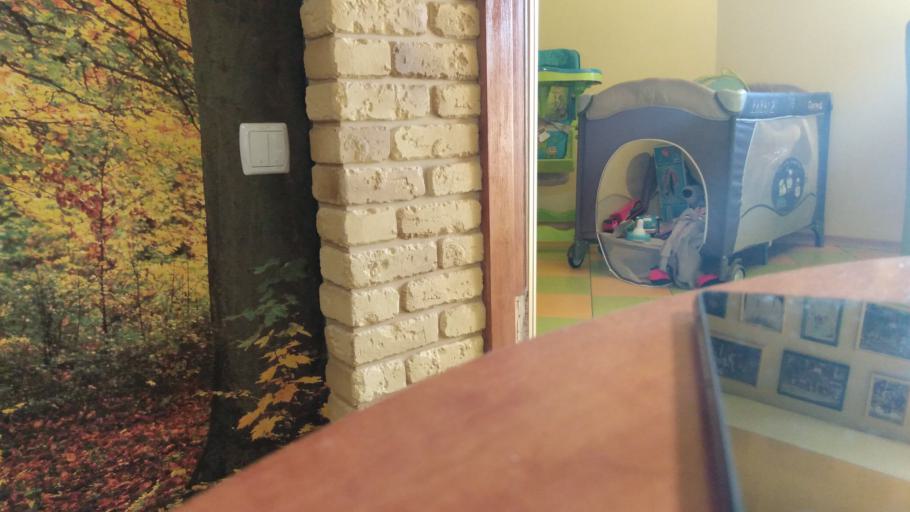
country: RU
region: Tverskaya
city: Bologoye
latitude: 57.9403
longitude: 34.1832
